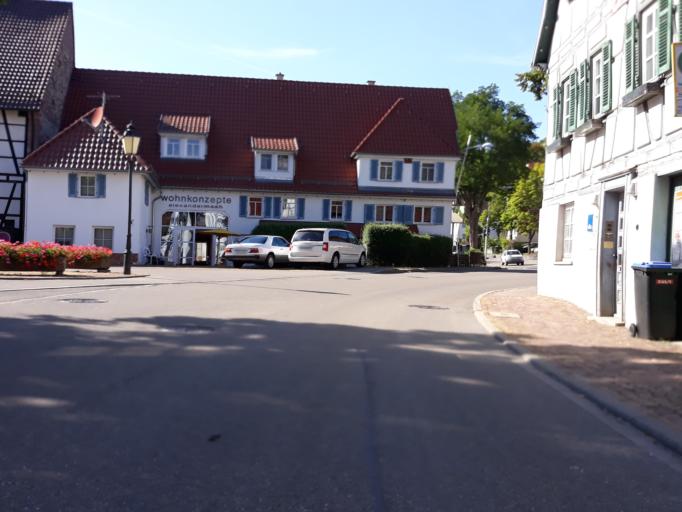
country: DE
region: Baden-Wuerttemberg
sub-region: Regierungsbezirk Stuttgart
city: Weil der Stadt
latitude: 48.7170
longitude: 8.8859
